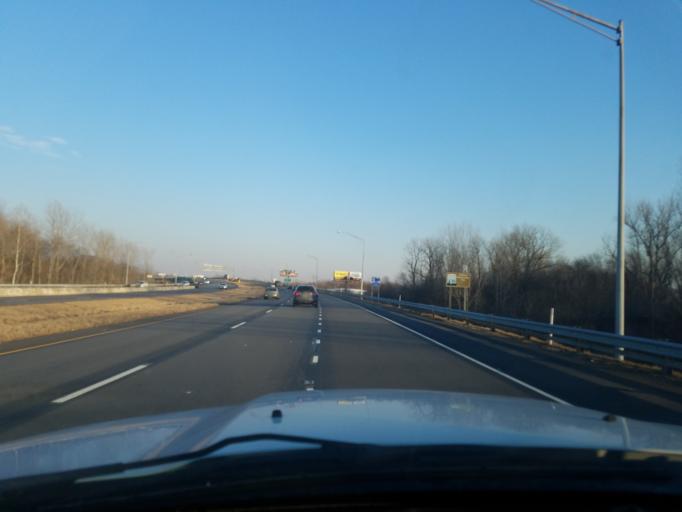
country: US
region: Indiana
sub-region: Vanderburgh County
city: Evansville
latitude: 37.9361
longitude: -87.5340
